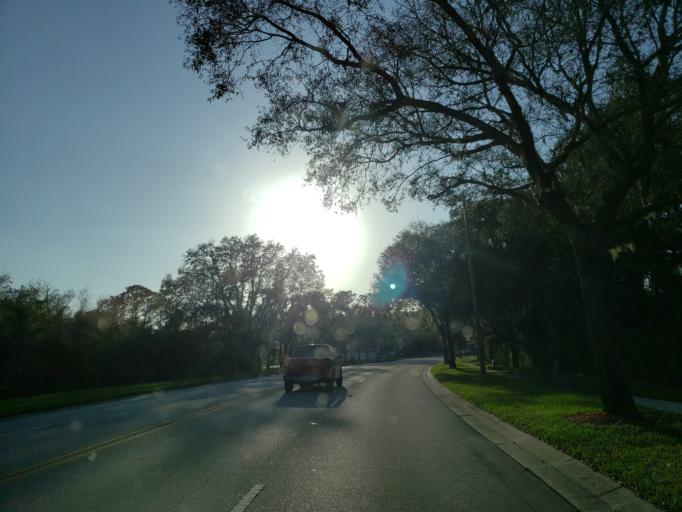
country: US
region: Florida
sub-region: Hillsborough County
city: Bloomingdale
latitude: 27.8760
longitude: -82.2672
